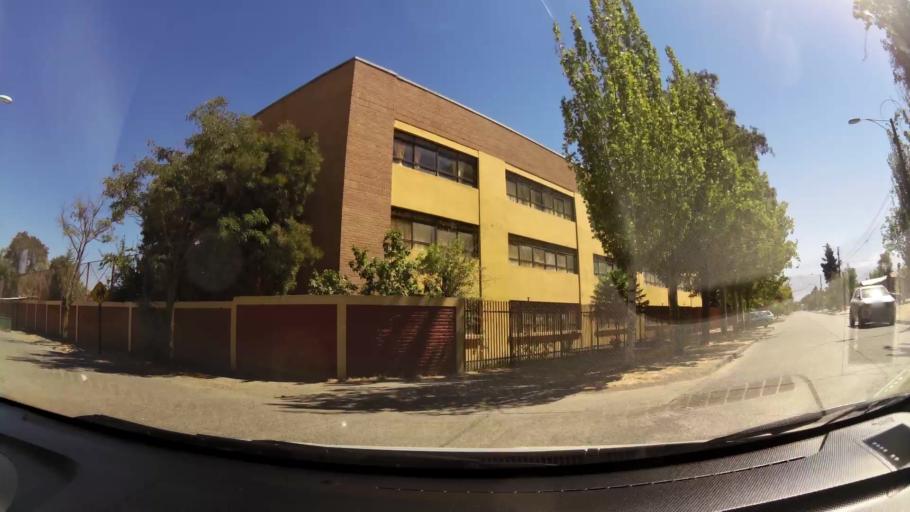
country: CL
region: O'Higgins
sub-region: Provincia de Cachapoal
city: Rancagua
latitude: -34.1766
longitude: -70.7173
